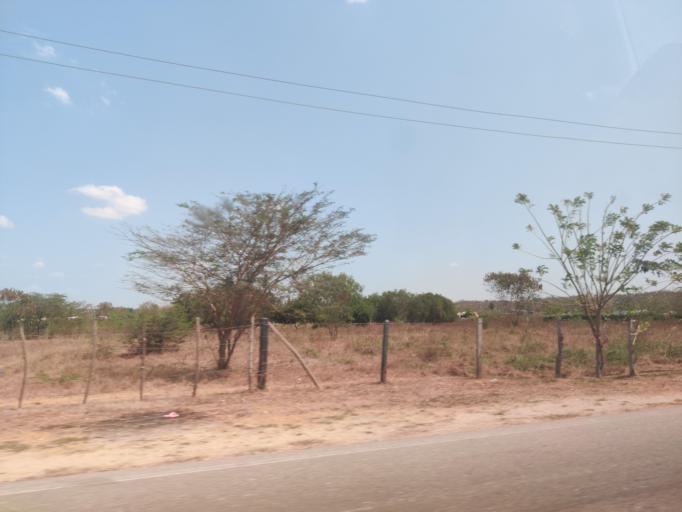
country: CO
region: Bolivar
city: Turbana
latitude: 10.2758
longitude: -75.5127
